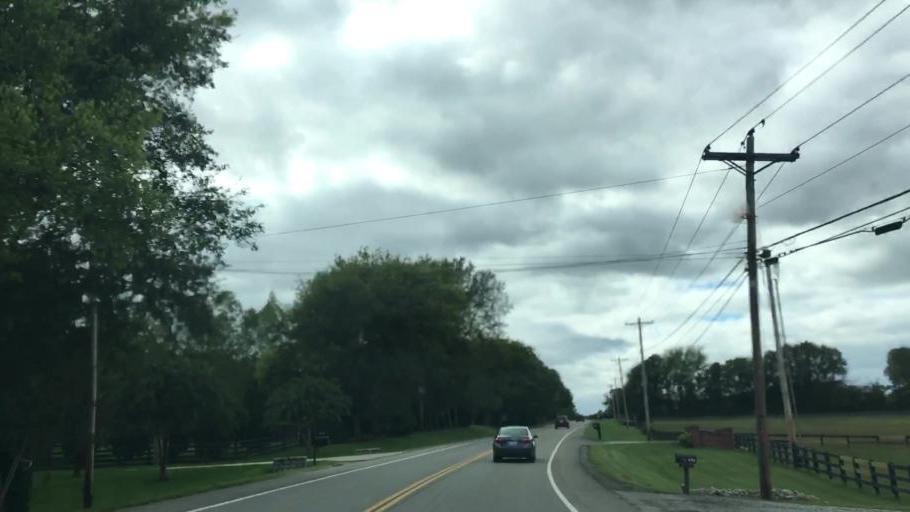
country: US
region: Tennessee
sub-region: Maury County
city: Columbia
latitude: 35.6131
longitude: -87.1299
